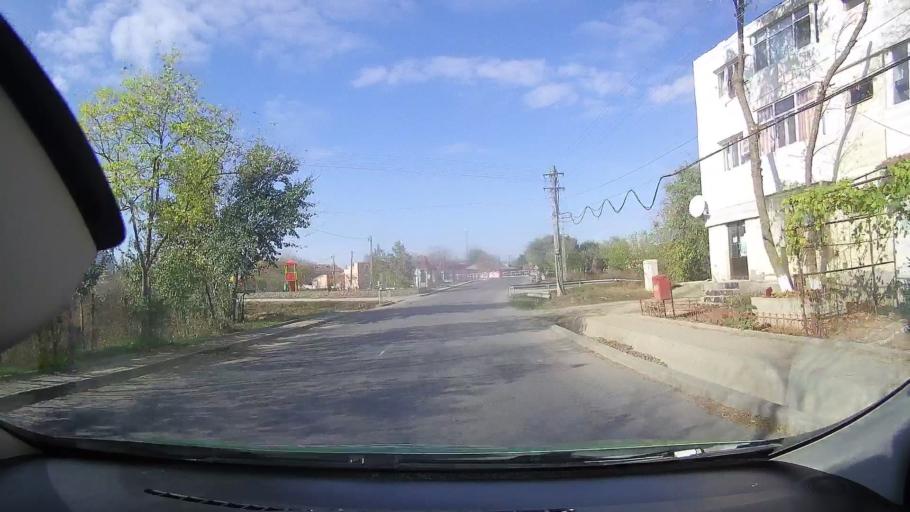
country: RO
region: Tulcea
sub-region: Comuna Valea Nucarilor
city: Valea Nucarilor
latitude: 45.0396
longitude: 28.9383
